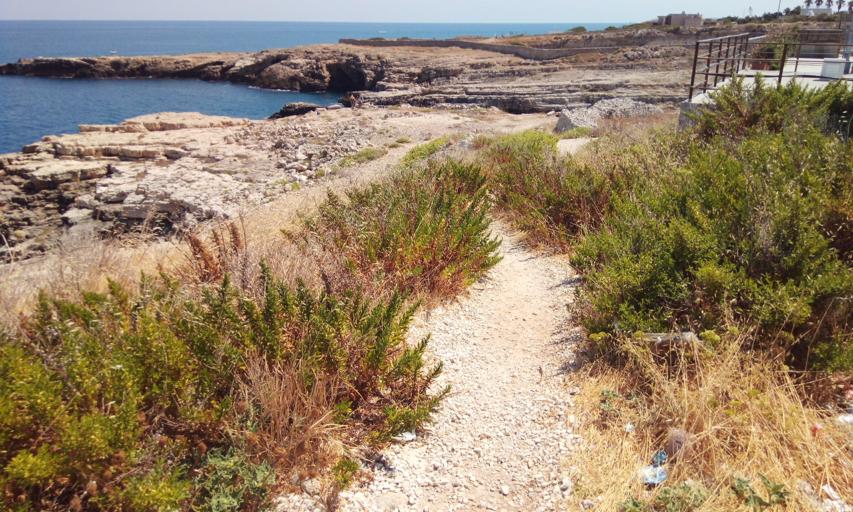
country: IT
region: Apulia
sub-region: Provincia di Bari
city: Polignano a Mare
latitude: 40.9925
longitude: 17.2327
